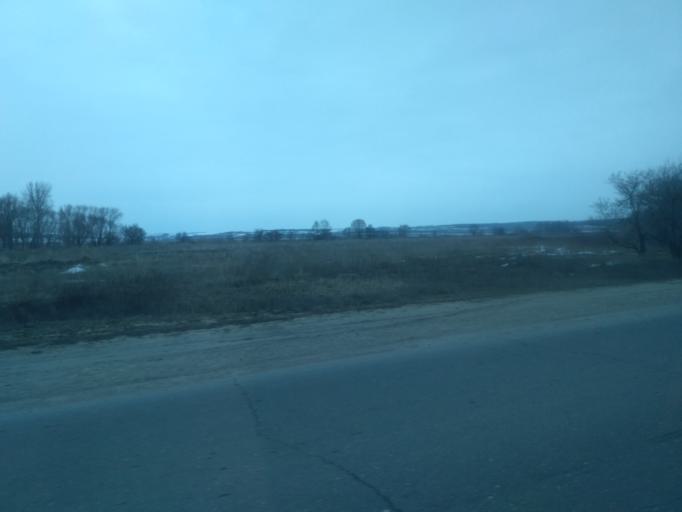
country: RU
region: Nizjnij Novgorod
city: Perevoz
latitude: 55.6022
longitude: 44.5455
